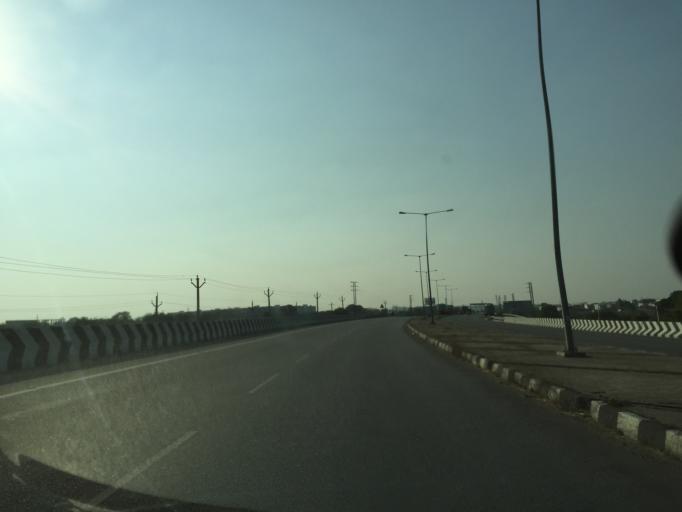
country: IN
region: Telangana
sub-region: Nalgonda
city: Bhongir
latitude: 17.4998
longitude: 78.8891
